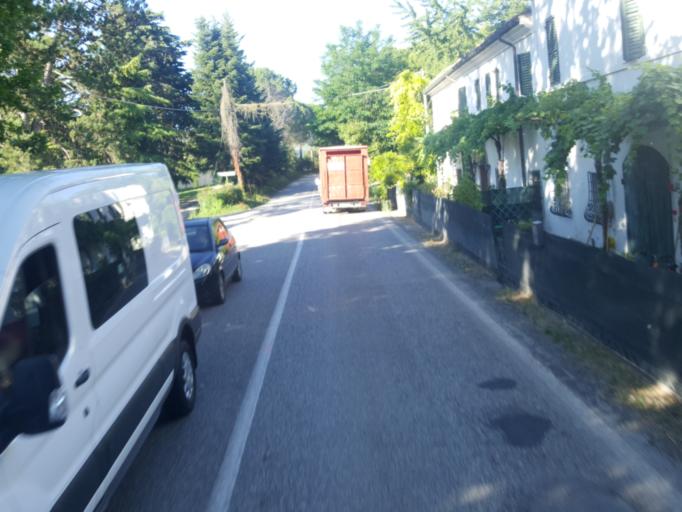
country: IT
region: The Marches
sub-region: Provincia di Pesaro e Urbino
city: Montecalvo in Foglia
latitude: 43.7939
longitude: 12.6500
